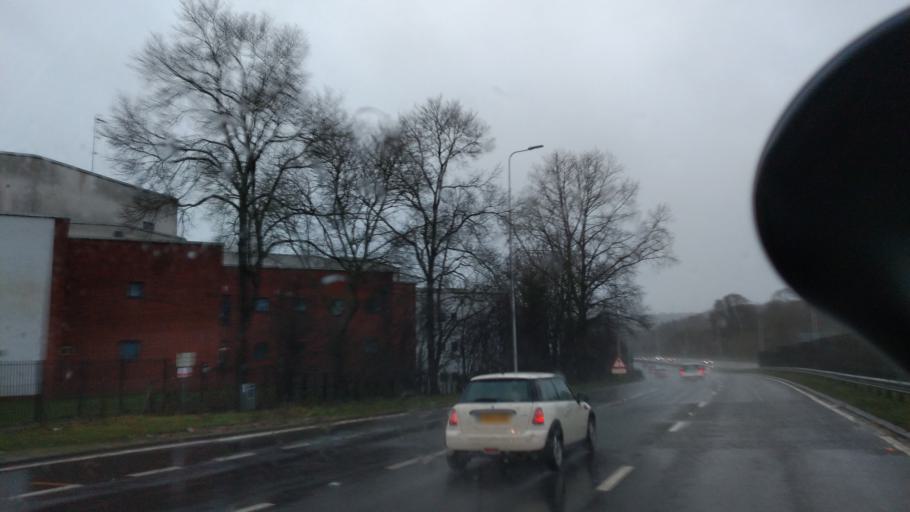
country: GB
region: England
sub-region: Brighton and Hove
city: Rottingdean
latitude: 50.8625
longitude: -0.0884
